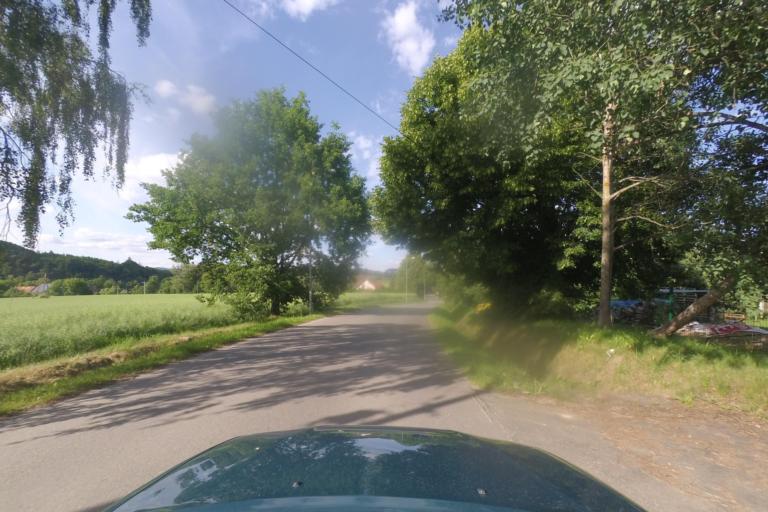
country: PL
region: Lower Silesian Voivodeship
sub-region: Powiat klodzki
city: Klodzko
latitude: 50.4758
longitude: 16.6650
